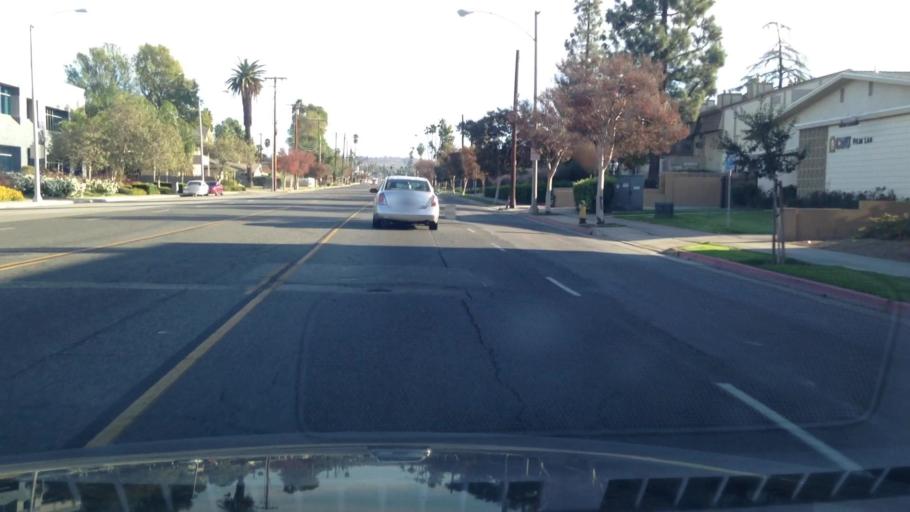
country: US
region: California
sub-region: Riverside County
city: Riverside
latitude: 33.9323
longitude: -117.4237
